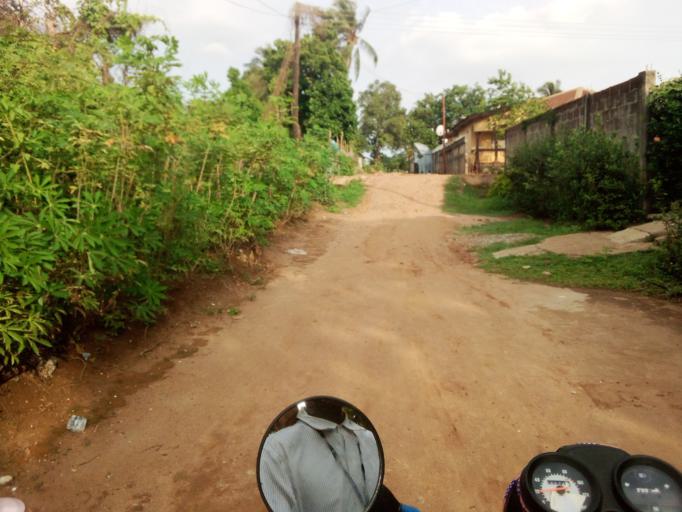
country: SL
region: Western Area
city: Waterloo
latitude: 8.3415
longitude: -13.0709
